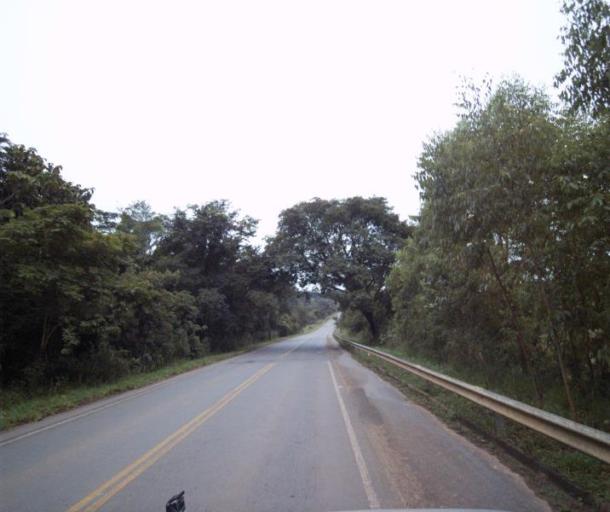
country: BR
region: Goias
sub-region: Pirenopolis
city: Pirenopolis
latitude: -15.9609
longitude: -48.8171
